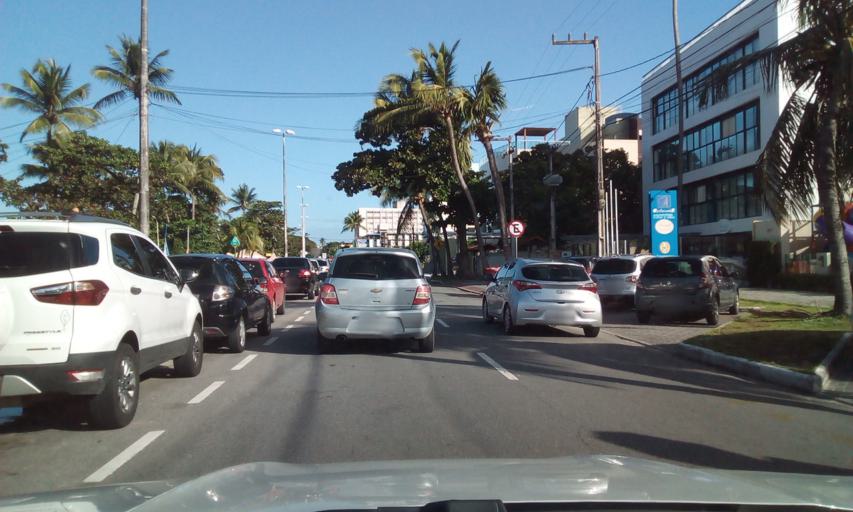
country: BR
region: Paraiba
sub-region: Joao Pessoa
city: Joao Pessoa
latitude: -7.1263
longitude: -34.8236
